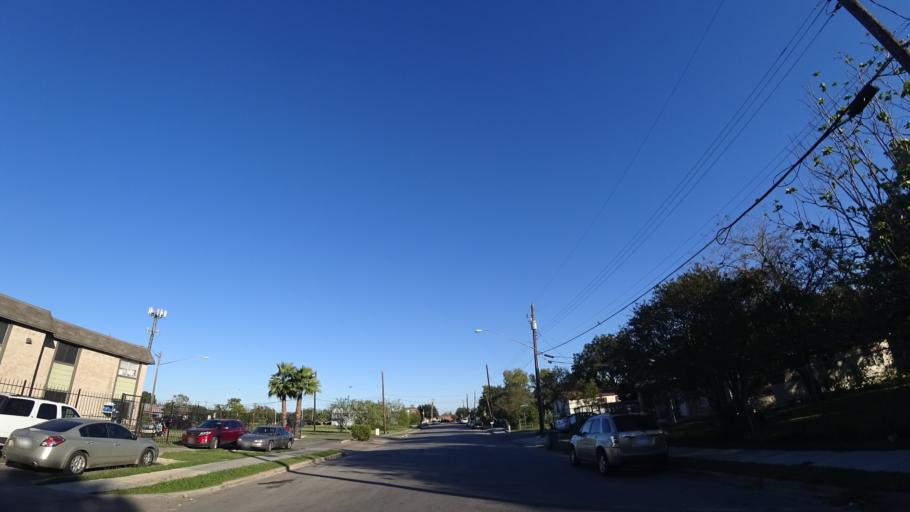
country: US
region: Texas
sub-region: Travis County
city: Austin
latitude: 30.2288
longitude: -97.7033
